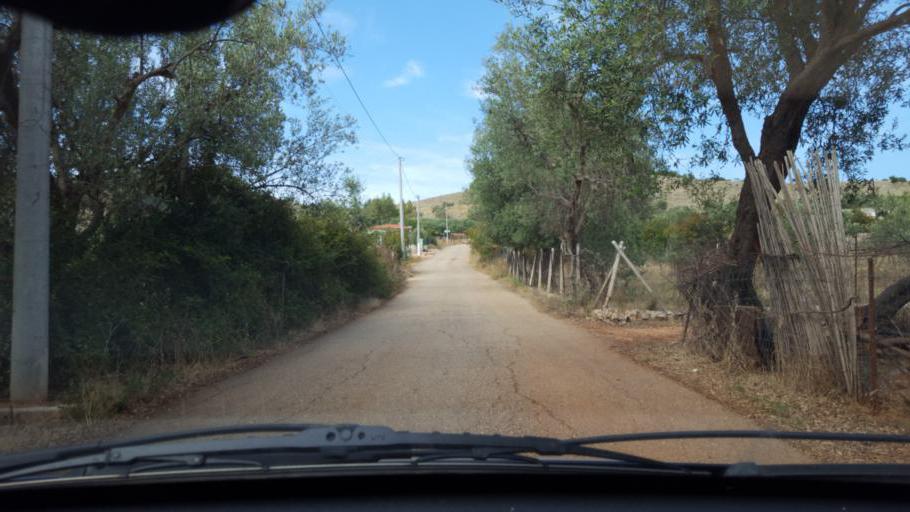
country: AL
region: Vlore
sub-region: Rrethi i Sarandes
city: Xarre
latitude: 39.7621
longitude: 19.9909
